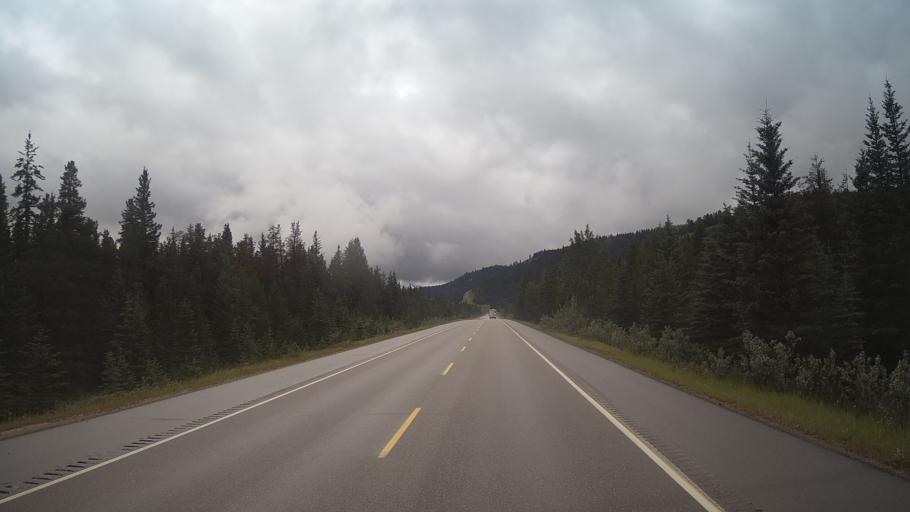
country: CA
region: Alberta
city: Jasper Park Lodge
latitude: 52.9257
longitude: -118.0416
